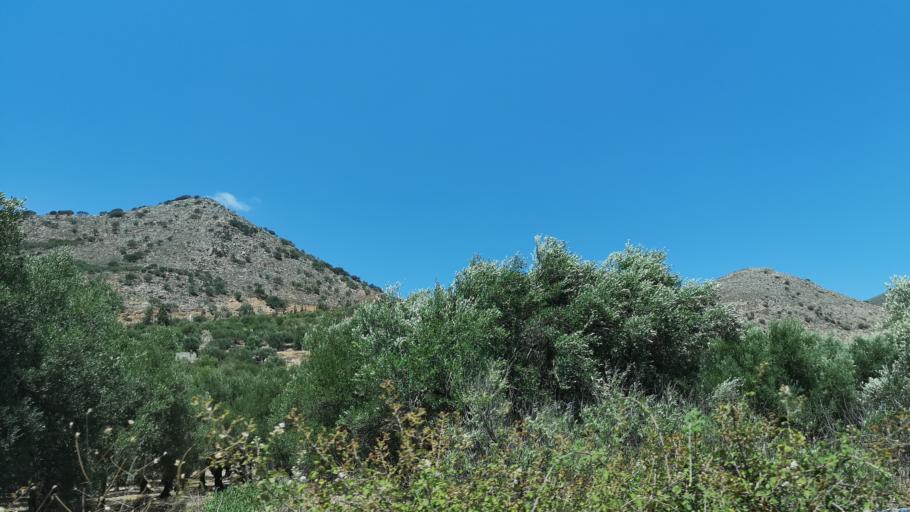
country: GR
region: Crete
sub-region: Nomos Lasithiou
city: Neapoli
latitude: 35.2480
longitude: 25.6263
